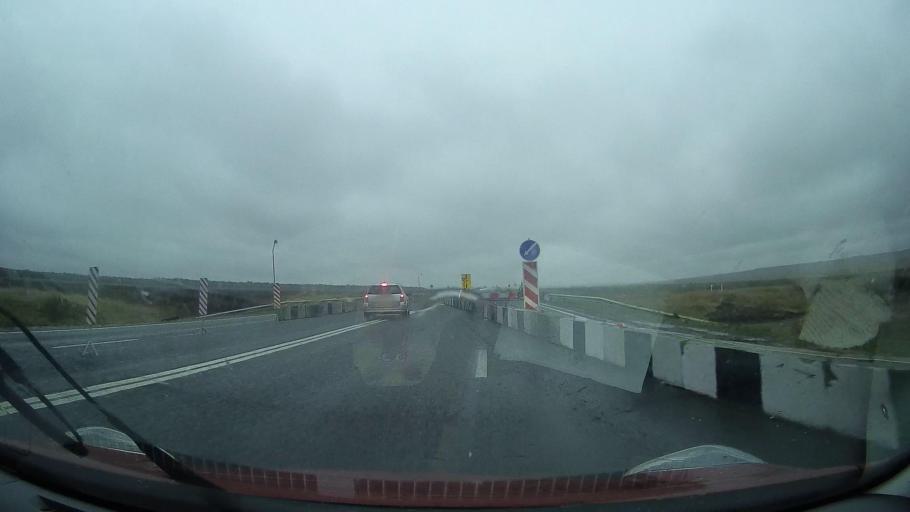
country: RU
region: Stavropol'skiy
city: Nevinnomyssk
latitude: 44.6257
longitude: 42.0575
